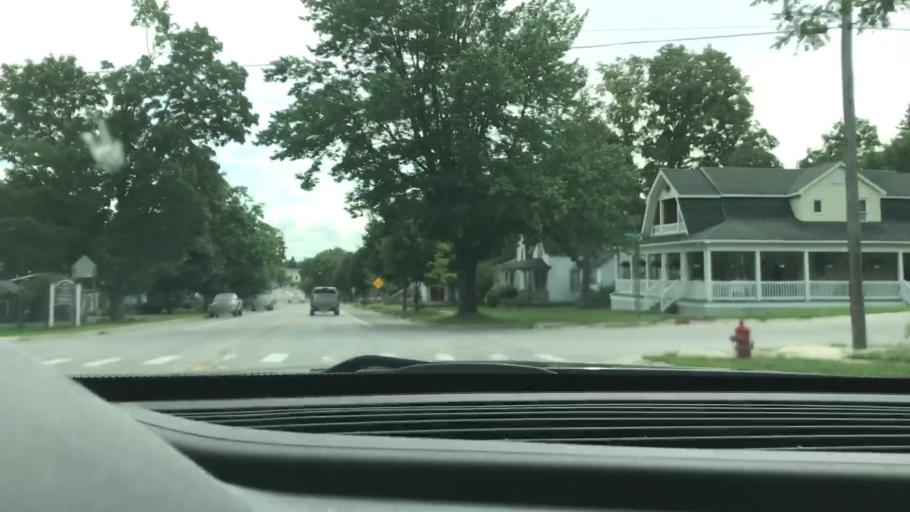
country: US
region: Michigan
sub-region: Antrim County
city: Bellaire
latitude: 44.9816
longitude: -85.2103
